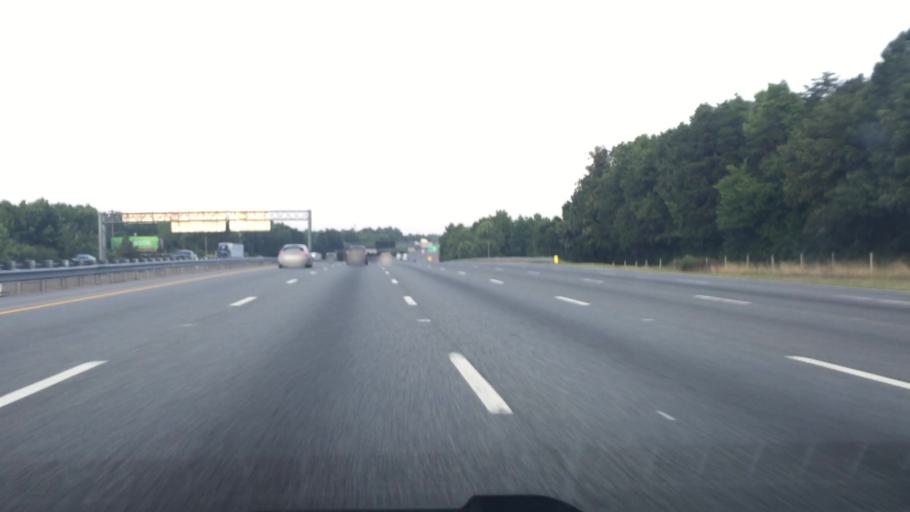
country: US
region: North Carolina
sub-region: Guilford County
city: Jamestown
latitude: 35.9962
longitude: -79.8668
